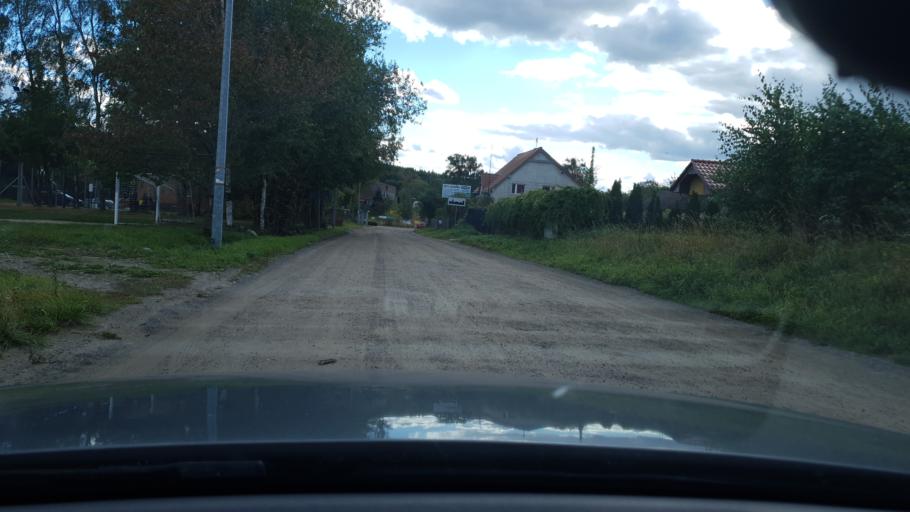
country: PL
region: Pomeranian Voivodeship
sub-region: Powiat wejherowski
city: Reda
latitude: 54.5753
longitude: 18.3093
